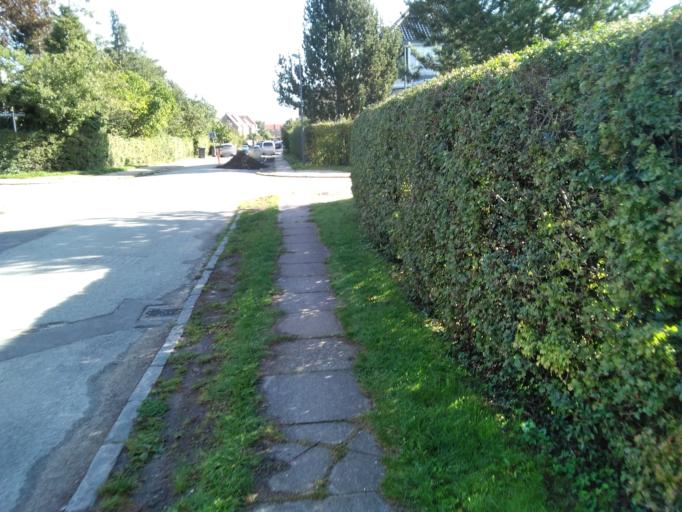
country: DK
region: Capital Region
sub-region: Kobenhavn
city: Vanlose
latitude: 55.6907
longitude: 12.5073
